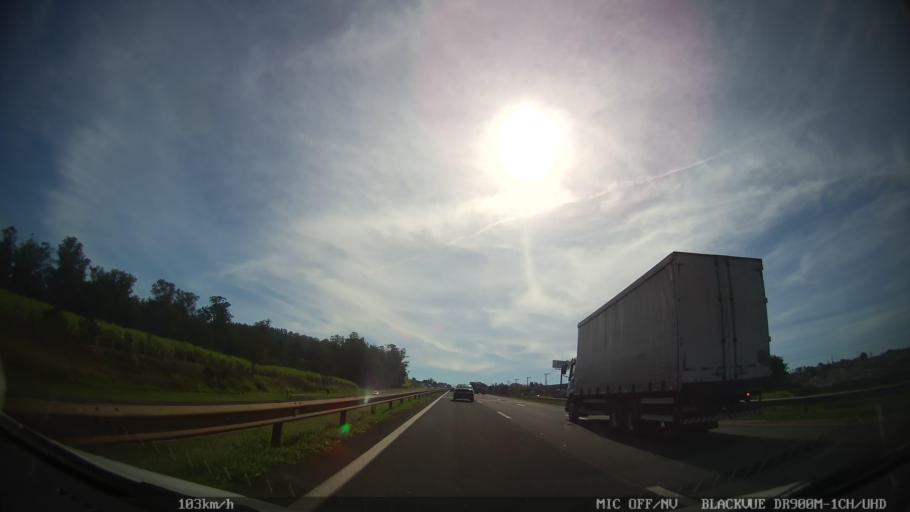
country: BR
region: Sao Paulo
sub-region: Araras
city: Araras
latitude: -22.3398
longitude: -47.3915
